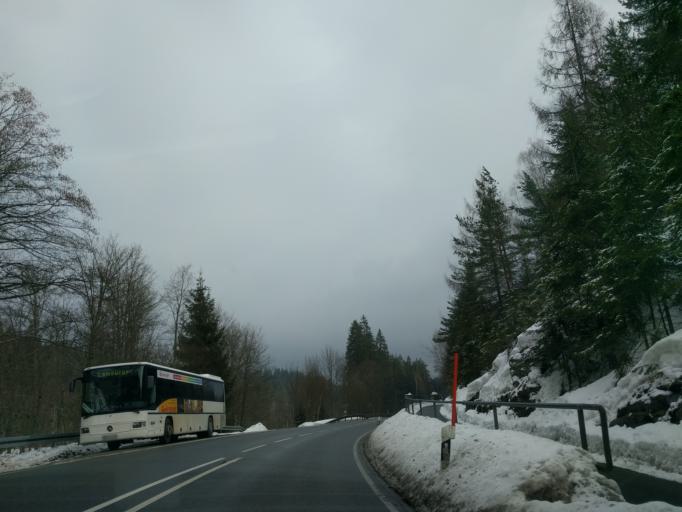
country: DE
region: Bavaria
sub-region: Lower Bavaria
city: Lindberg
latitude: 49.0438
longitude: 13.2263
